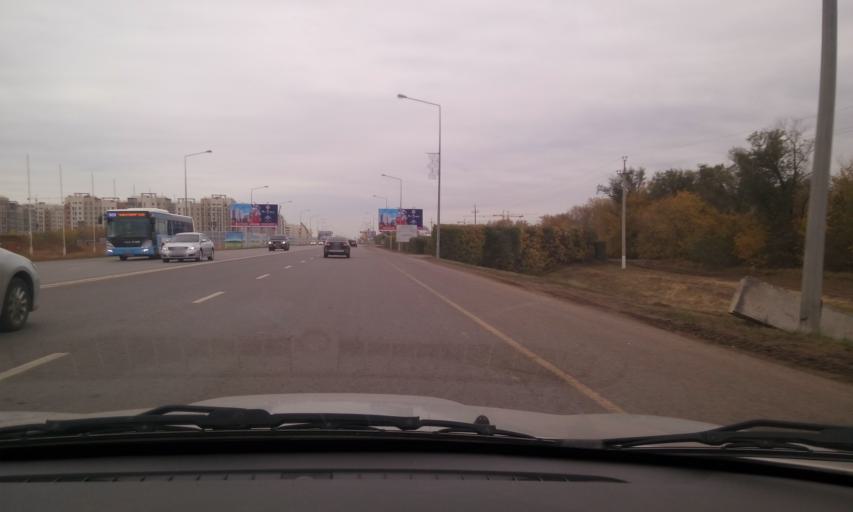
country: KZ
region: Astana Qalasy
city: Astana
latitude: 51.1024
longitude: 71.4072
